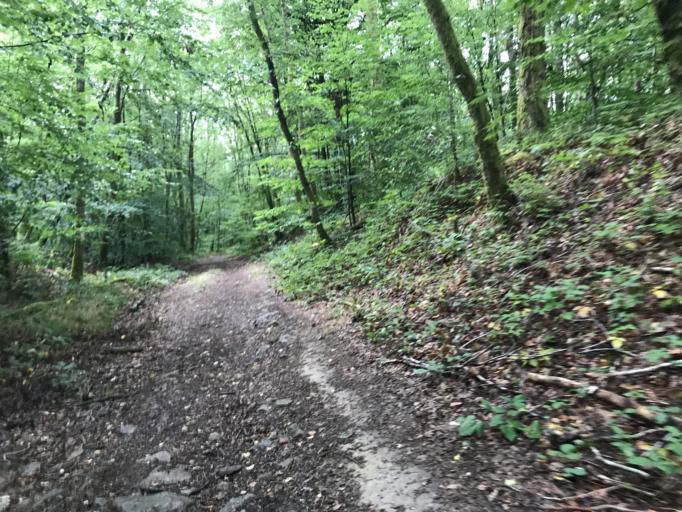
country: FR
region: Champagne-Ardenne
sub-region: Departement des Ardennes
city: Thilay
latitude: 49.8783
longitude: 4.7904
